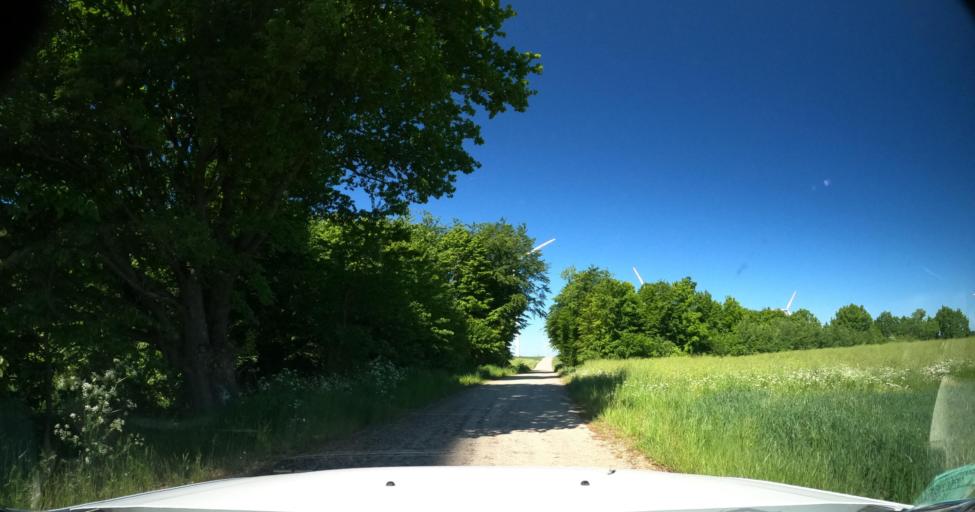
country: PL
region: Pomeranian Voivodeship
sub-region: Powiat slupski
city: Ustka
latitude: 54.5095
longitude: 16.7522
